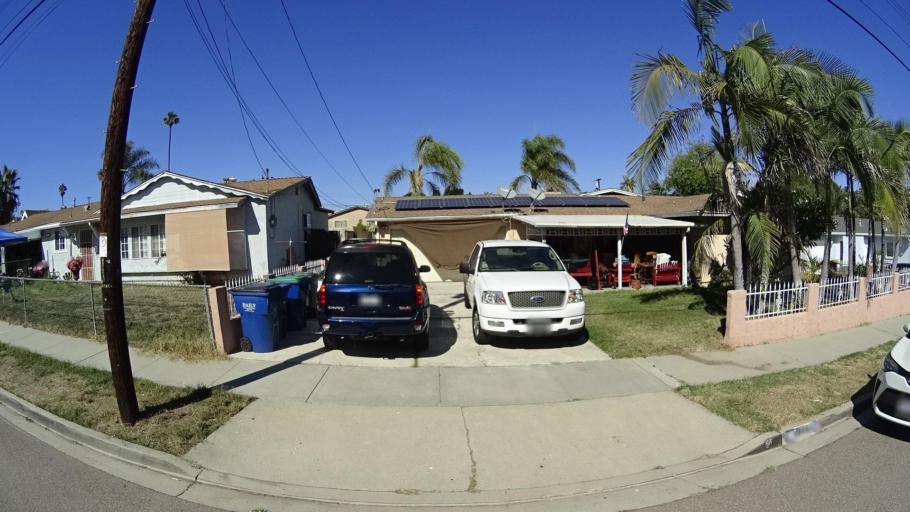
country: US
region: California
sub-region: San Diego County
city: La Presa
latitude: 32.7192
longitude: -117.0165
